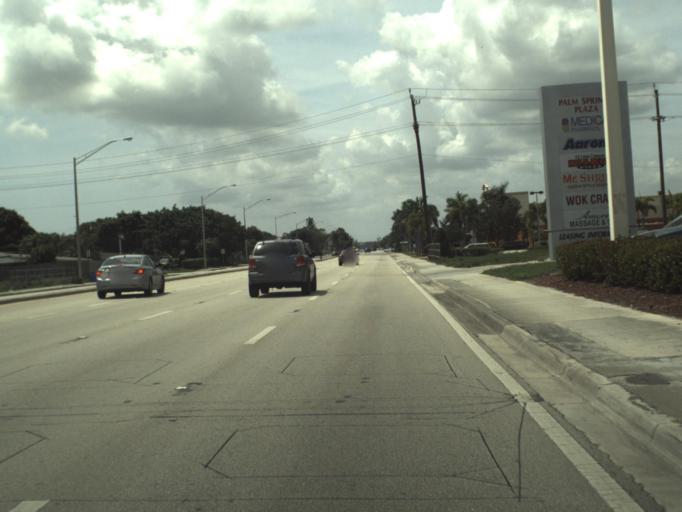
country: US
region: Florida
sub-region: Palm Beach County
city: Palm Springs
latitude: 26.6255
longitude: -80.0889
